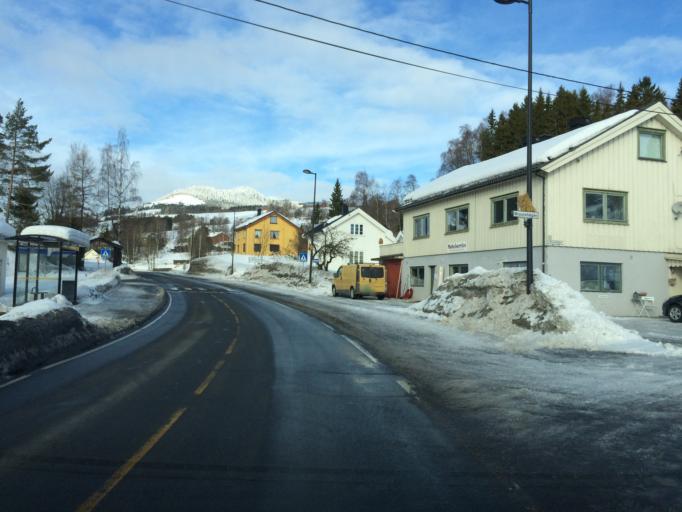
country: NO
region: Oppland
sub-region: Gausdal
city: Segalstad bru
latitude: 61.2178
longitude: 10.2774
